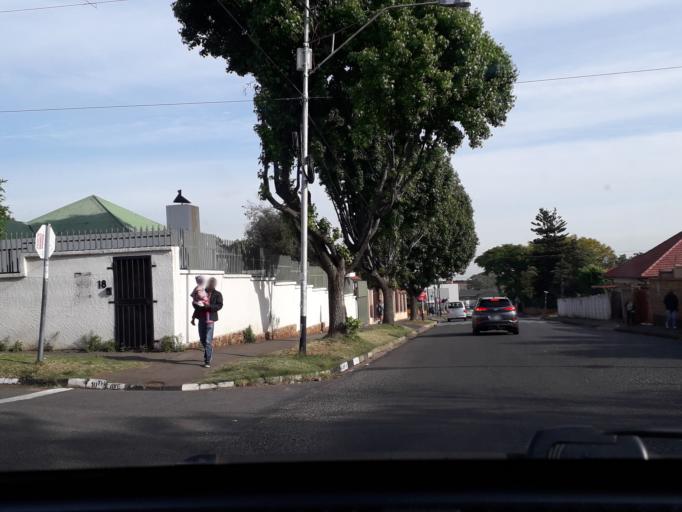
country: ZA
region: Gauteng
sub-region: City of Johannesburg Metropolitan Municipality
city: Johannesburg
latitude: -26.1407
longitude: 28.0886
